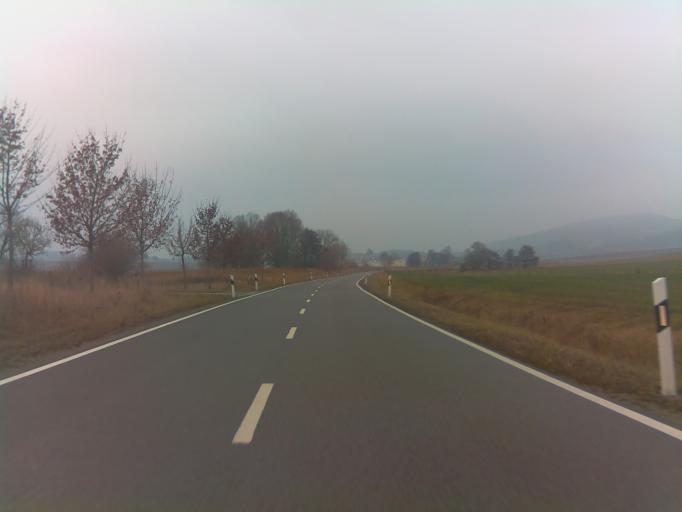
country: DE
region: Thuringia
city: Romhild
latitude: 50.4226
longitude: 10.5210
